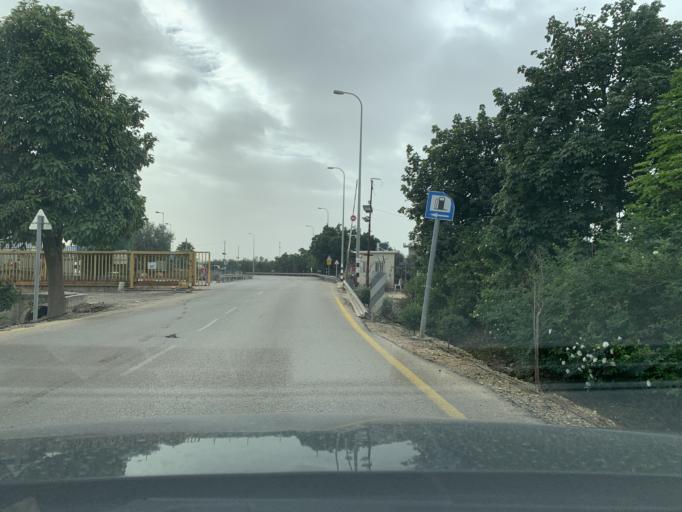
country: IL
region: Central District
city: Jaljulya
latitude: 32.1561
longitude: 34.9466
